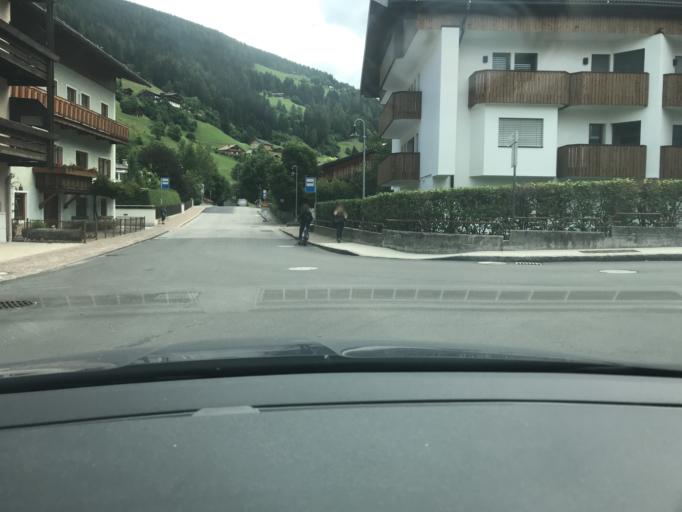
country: IT
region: Trentino-Alto Adige
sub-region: Bolzano
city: San Candido
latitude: 46.7343
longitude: 12.2844
